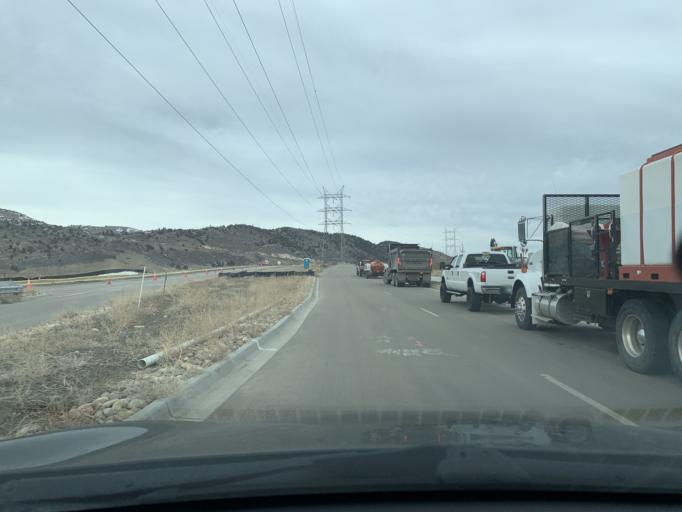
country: US
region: Colorado
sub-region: Jefferson County
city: West Pleasant View
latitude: 39.6712
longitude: -105.1804
